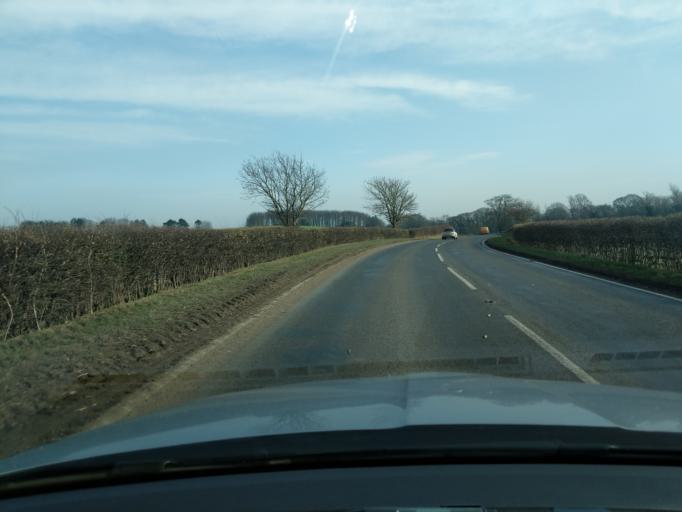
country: GB
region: England
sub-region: North Yorkshire
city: Bedale
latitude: 54.3092
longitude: -1.6481
